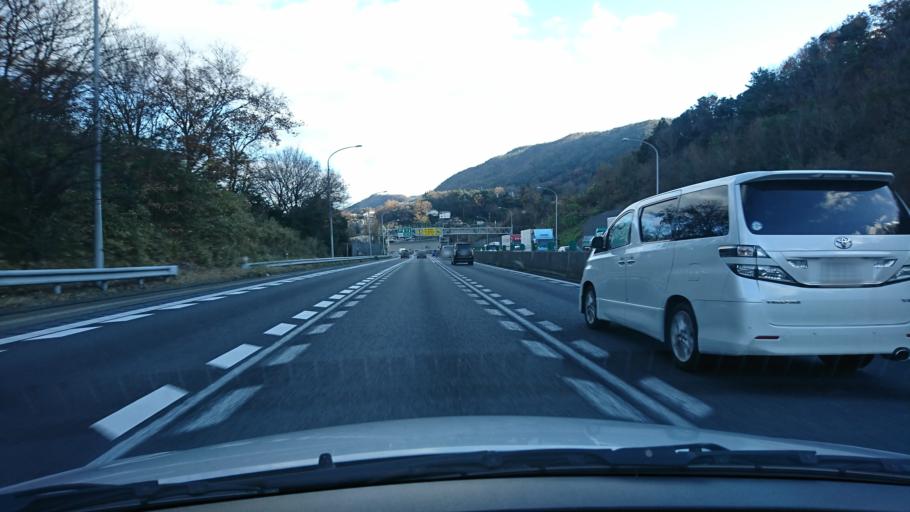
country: JP
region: Hyogo
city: Sandacho
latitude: 34.8325
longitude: 135.2834
